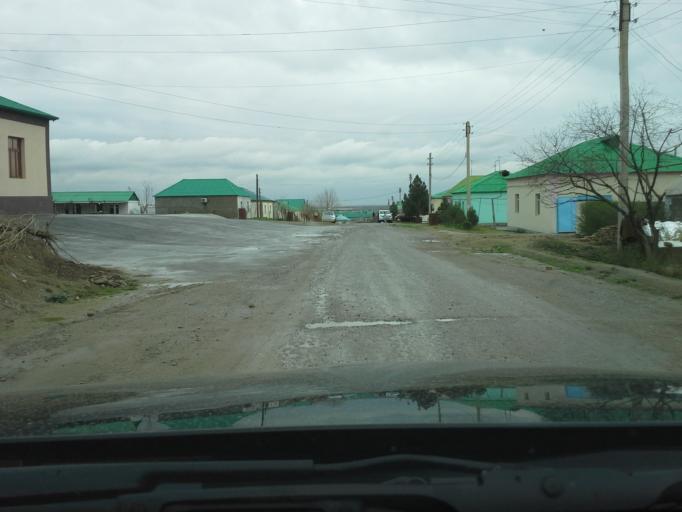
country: TM
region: Ahal
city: Abadan
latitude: 37.9636
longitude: 58.2030
